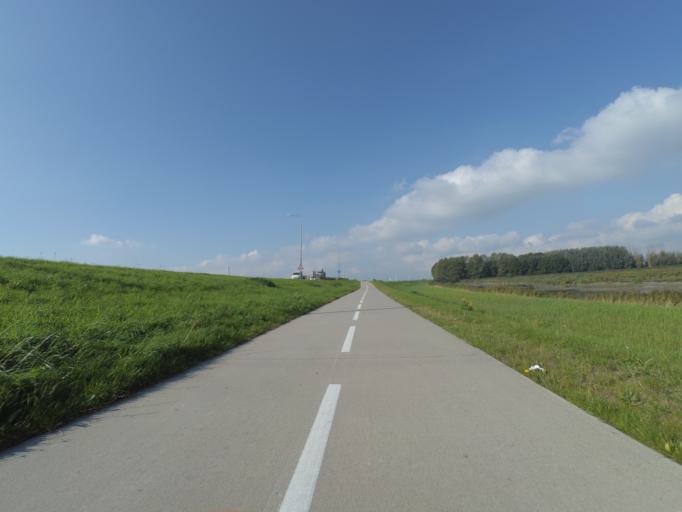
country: NL
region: Flevoland
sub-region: Gemeente Zeewolde
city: Zeewolde
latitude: 52.3672
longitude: 5.5658
